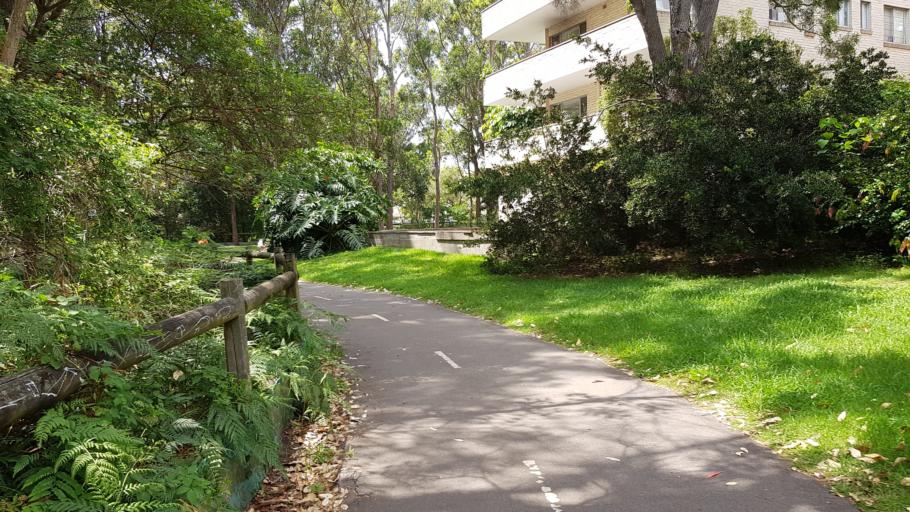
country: AU
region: New South Wales
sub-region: Warringah
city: Dee Why
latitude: -33.7504
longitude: 151.2926
